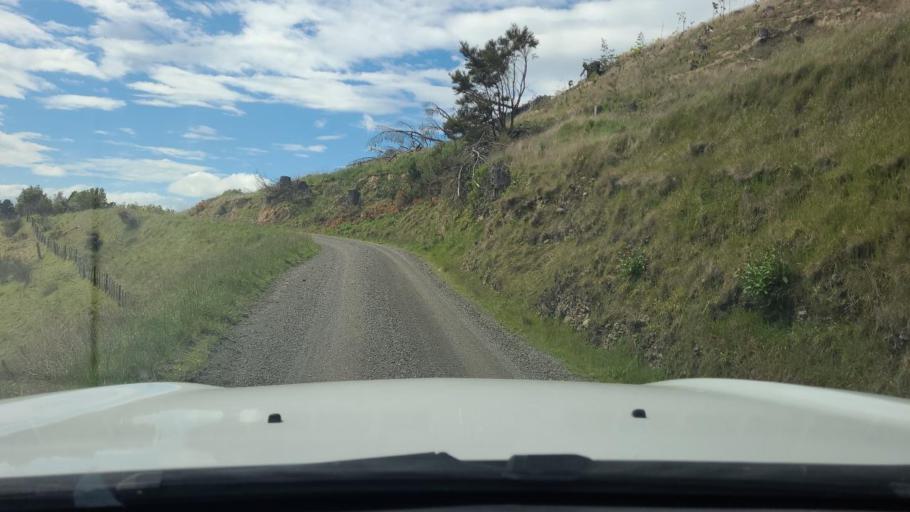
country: NZ
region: Wellington
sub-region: South Wairarapa District
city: Waipawa
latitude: -41.3453
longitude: 175.4063
